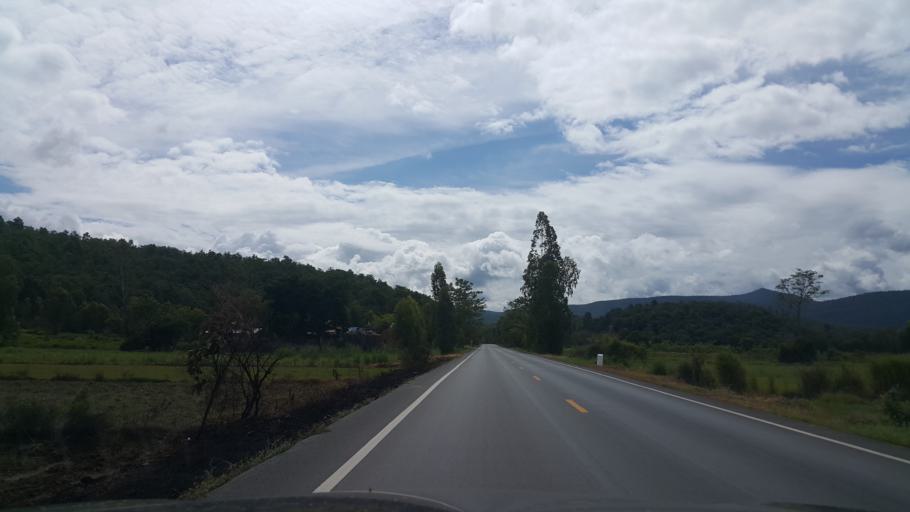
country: TH
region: Uttaradit
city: Thong Saen Khan
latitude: 17.3638
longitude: 100.2414
